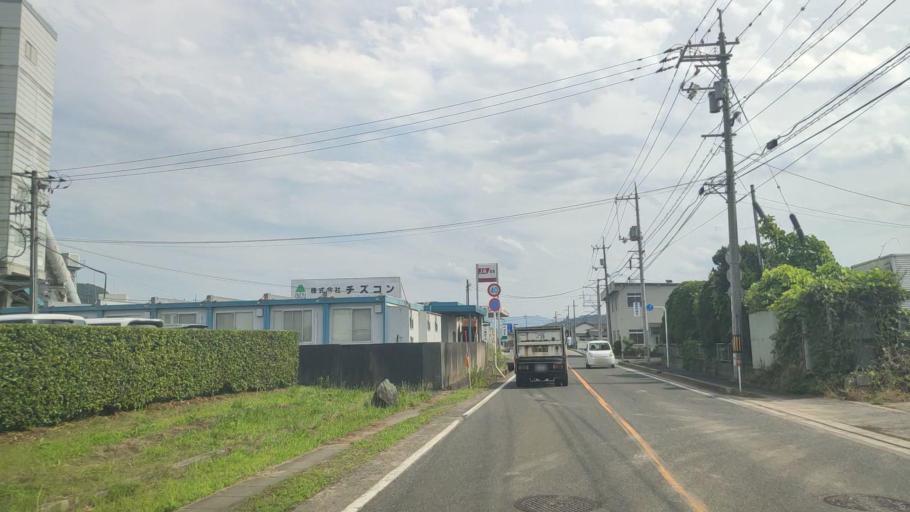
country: JP
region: Tottori
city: Tottori
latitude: 35.4653
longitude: 134.2036
